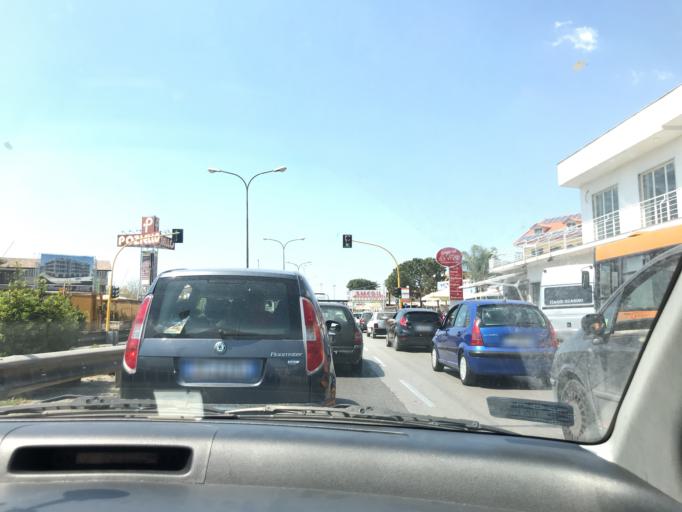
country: IT
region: Campania
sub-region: Provincia di Napoli
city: Villaricca
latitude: 40.9221
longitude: 14.1743
